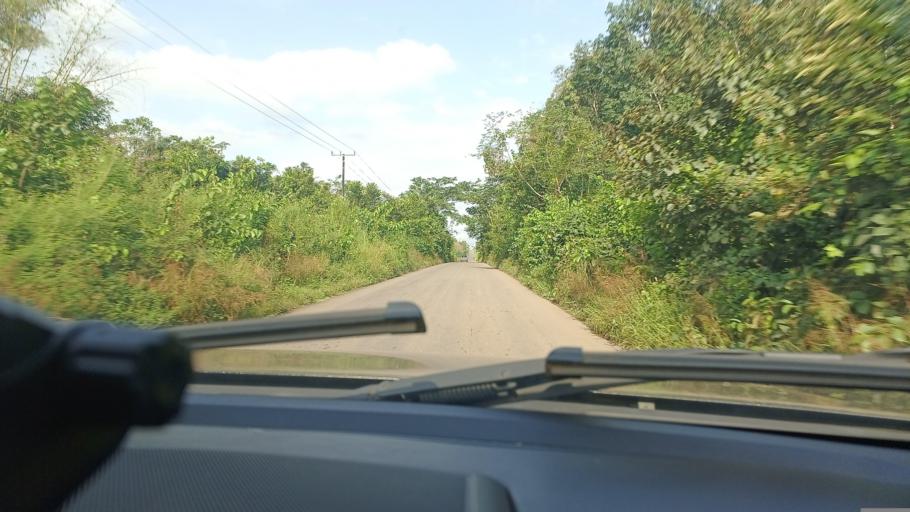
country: LR
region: Bomi
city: Tubmanburg
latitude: 6.6890
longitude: -10.8812
